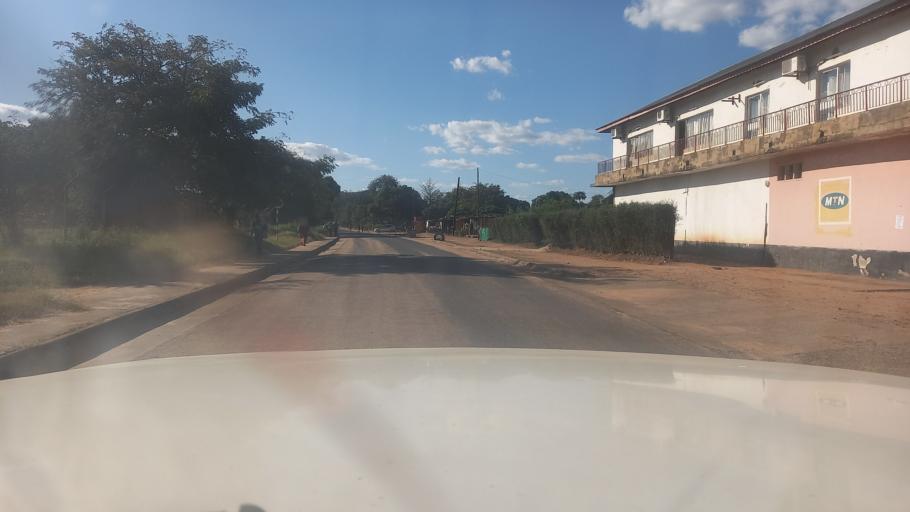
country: ZM
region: Southern
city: Livingstone
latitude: -17.8390
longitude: 25.8664
